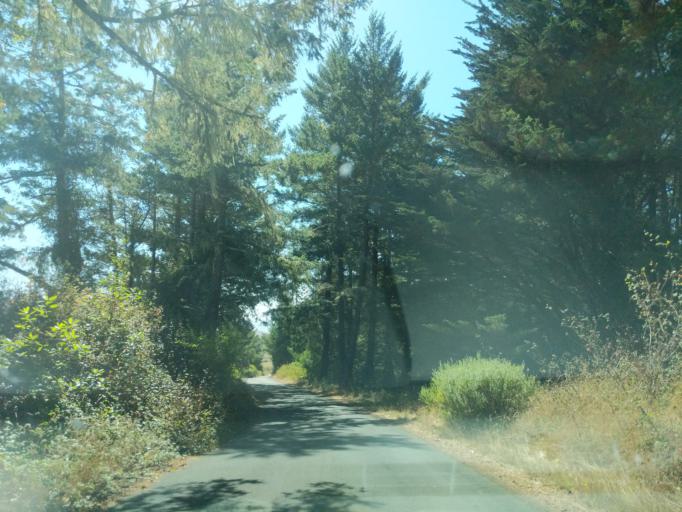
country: US
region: California
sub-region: Sonoma County
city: Monte Rio
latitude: 38.5219
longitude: -123.2431
